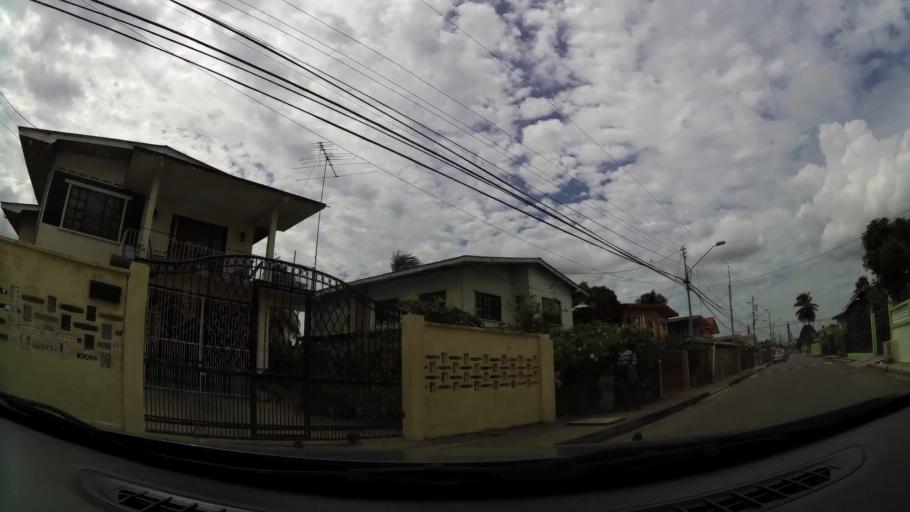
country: TT
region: Couva-Tabaquite-Talparo
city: Couva
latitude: 10.3980
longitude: -61.4680
